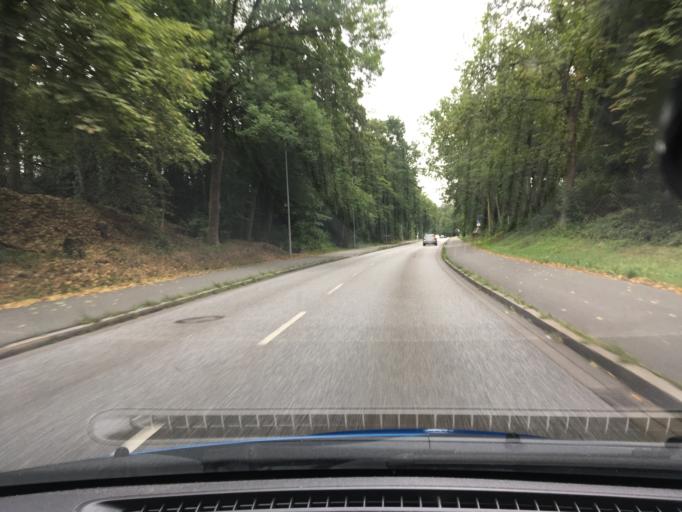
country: DE
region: Schleswig-Holstein
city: Geesthacht
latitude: 53.4336
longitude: 10.3882
